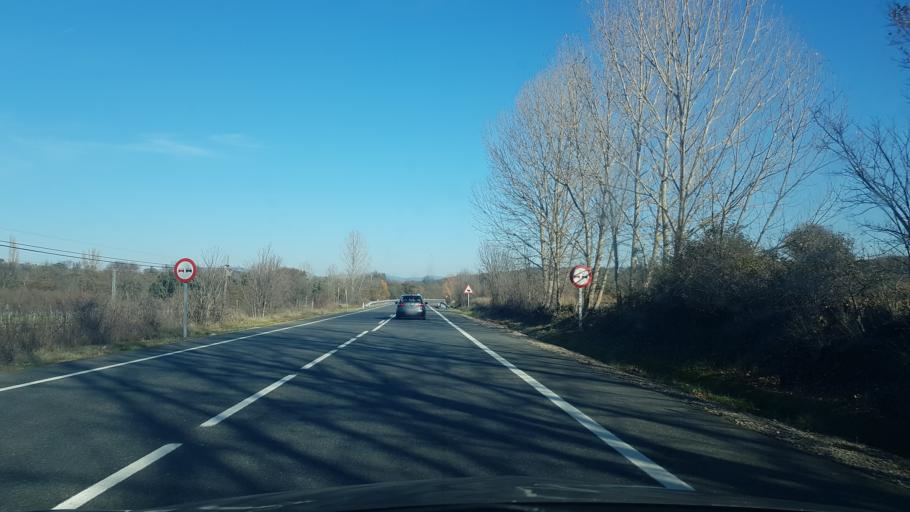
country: ES
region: Madrid
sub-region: Provincia de Madrid
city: Rozas de Puerto Real
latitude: 40.3423
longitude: -4.4560
